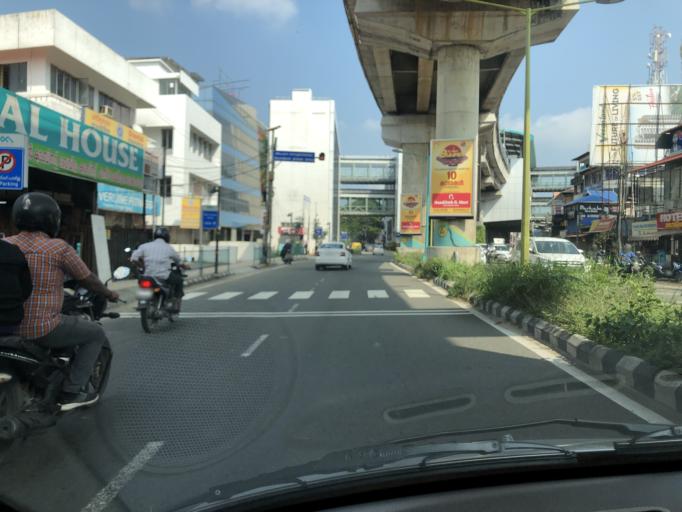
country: IN
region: Kerala
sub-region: Ernakulam
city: Elur
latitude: 10.0138
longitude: 76.3024
